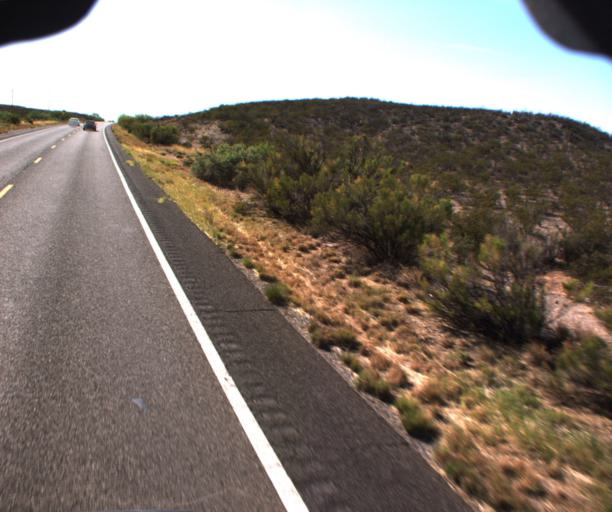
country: US
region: Arizona
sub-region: Cochise County
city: Tombstone
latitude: 31.7763
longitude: -110.1319
